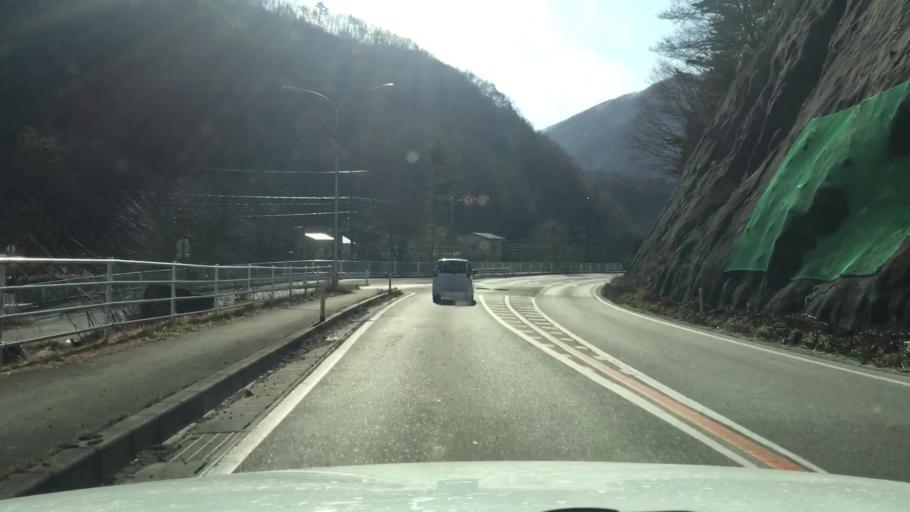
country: JP
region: Iwate
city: Miyako
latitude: 39.5937
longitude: 141.6752
